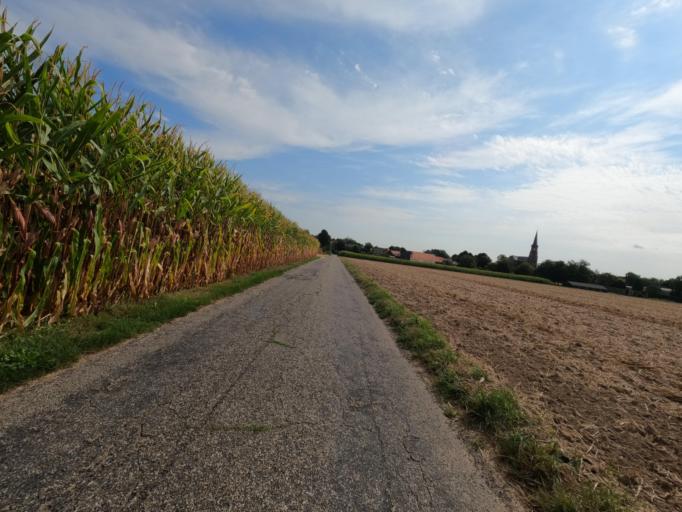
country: DE
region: North Rhine-Westphalia
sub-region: Regierungsbezirk Koln
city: Waldfeucht
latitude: 51.0588
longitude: 6.0354
